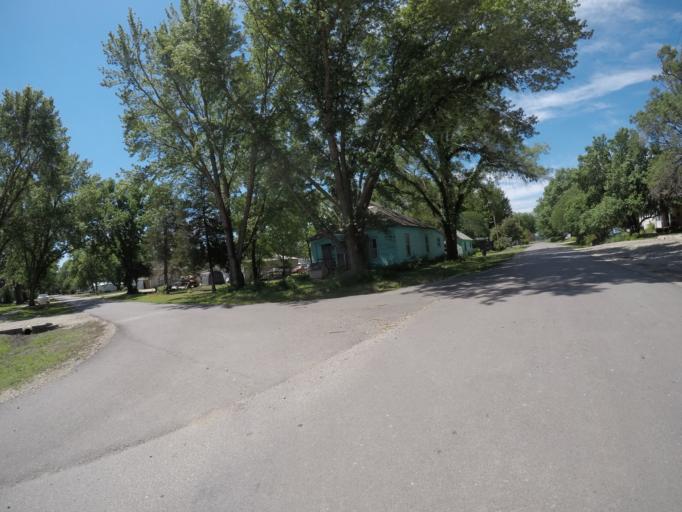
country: US
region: Kansas
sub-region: Wabaunsee County
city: Alma
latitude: 39.0536
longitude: -96.2398
